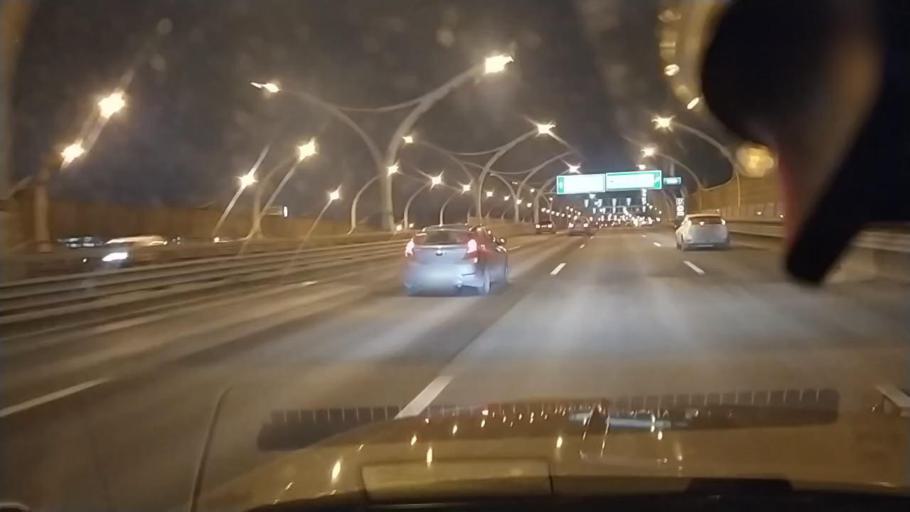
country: RU
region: St.-Petersburg
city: Staraya Derevnya
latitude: 59.9874
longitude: 30.2303
